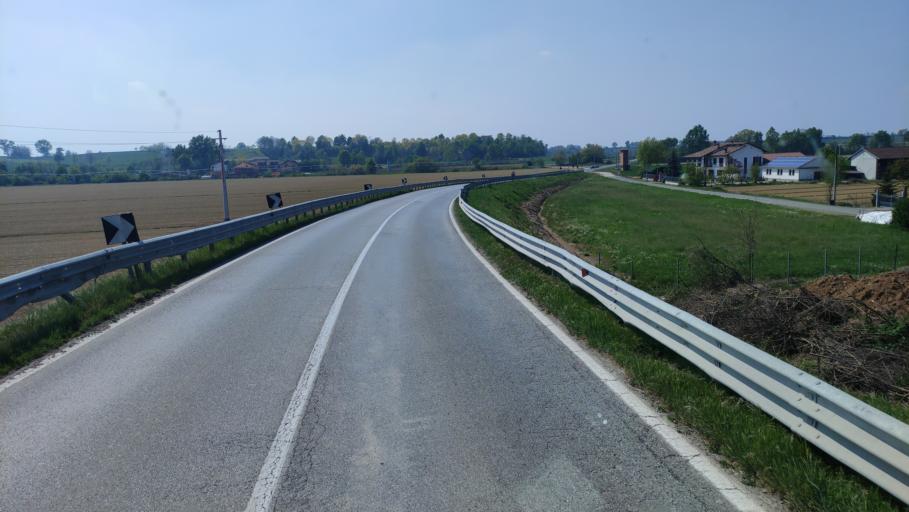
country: IT
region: Piedmont
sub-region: Provincia di Cuneo
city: Cervere
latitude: 44.6642
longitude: 7.7737
